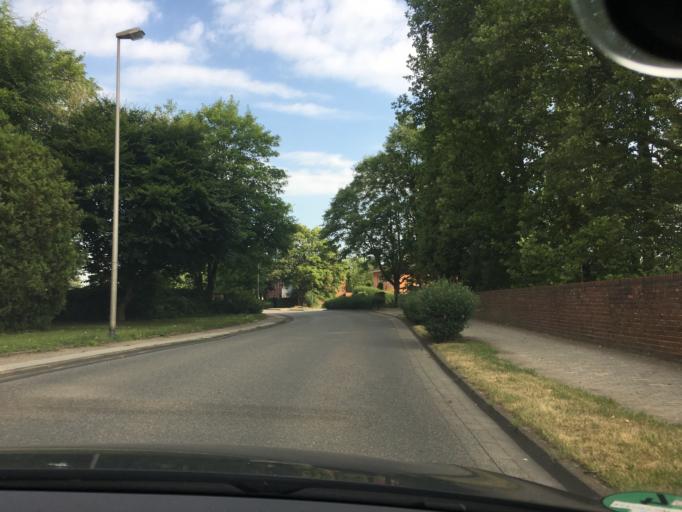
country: DE
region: North Rhine-Westphalia
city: Julich
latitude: 50.8997
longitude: 6.3520
